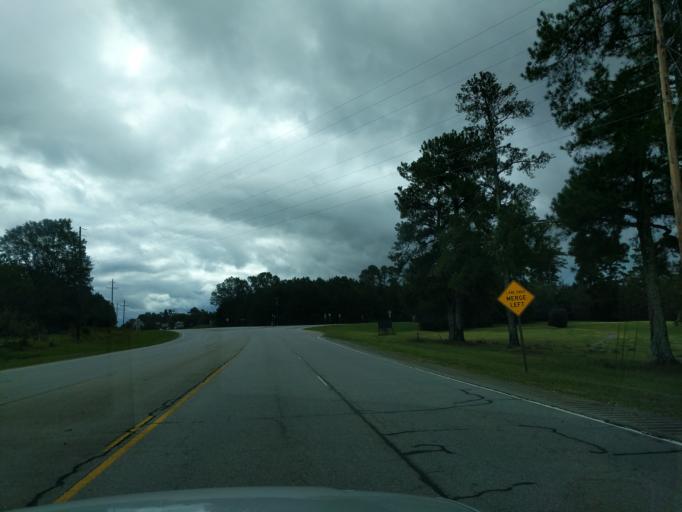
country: US
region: Georgia
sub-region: Wilkes County
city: Washington
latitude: 33.6998
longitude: -82.6895
